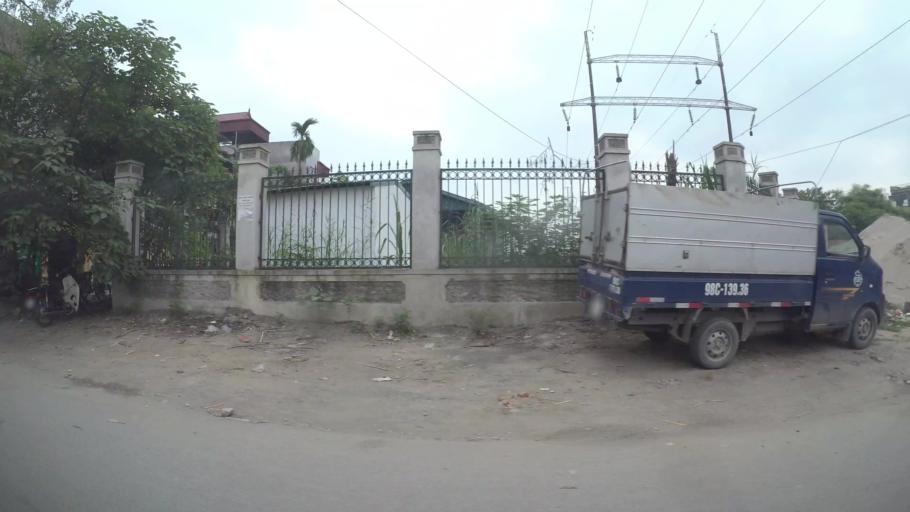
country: VN
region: Ha Noi
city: Cau Dien
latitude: 21.0348
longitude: 105.7478
